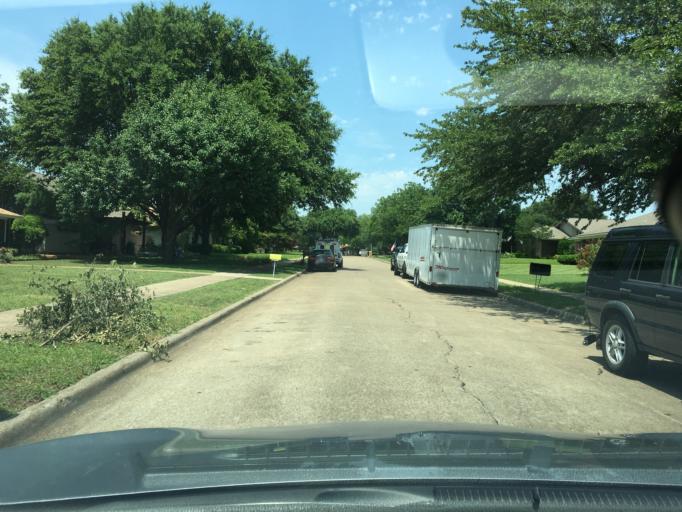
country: US
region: Texas
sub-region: Dallas County
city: Richardson
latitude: 32.9621
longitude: -96.6884
